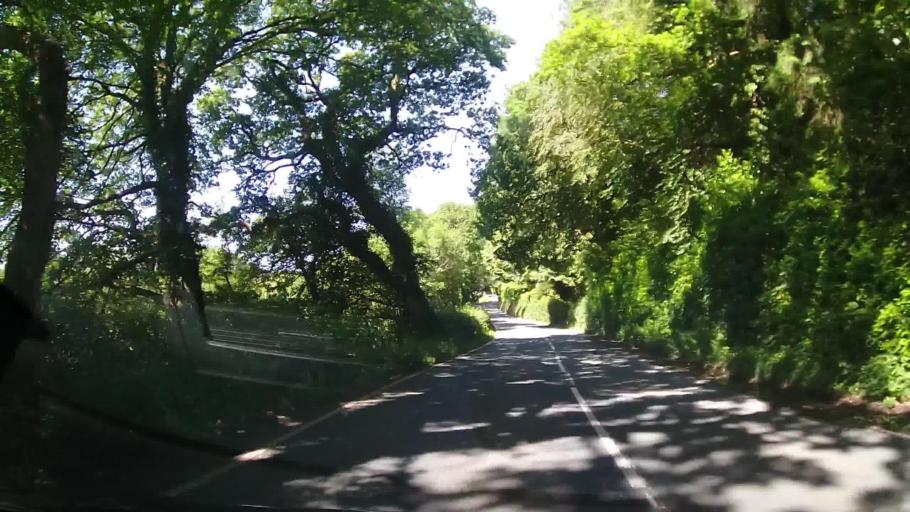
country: GB
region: Wales
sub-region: Sir Powys
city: Machynlleth
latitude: 52.5951
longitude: -3.8703
